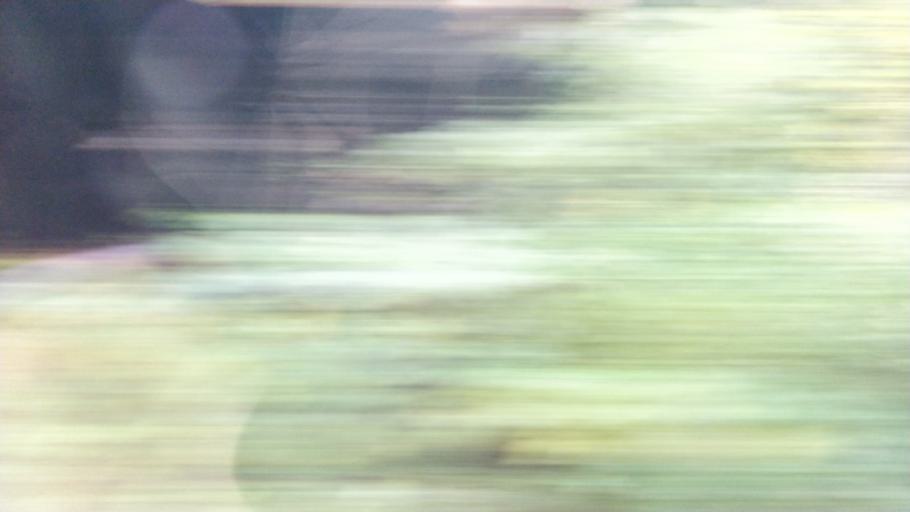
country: GB
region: England
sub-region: Borough of Bolton
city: Westhoughton
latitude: 53.5430
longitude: -2.5370
